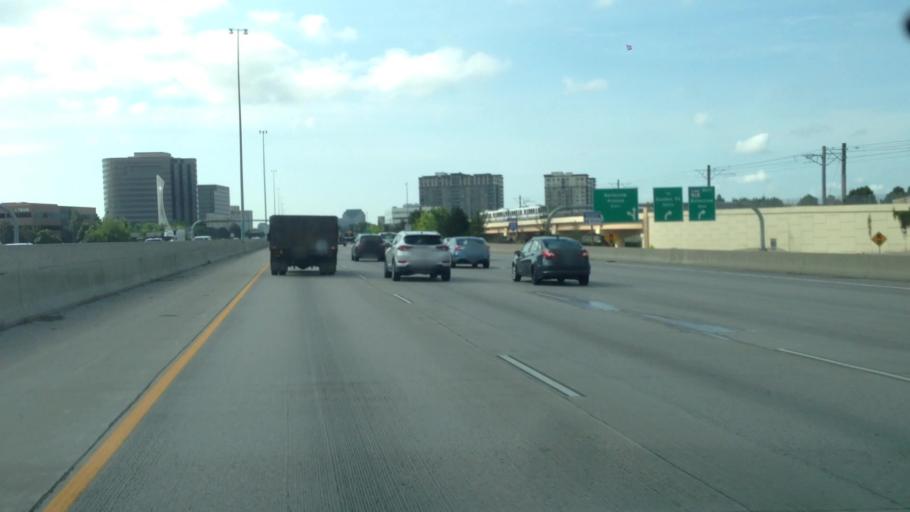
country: US
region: Colorado
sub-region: Arapahoe County
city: Castlewood
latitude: 39.6260
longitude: -104.9035
